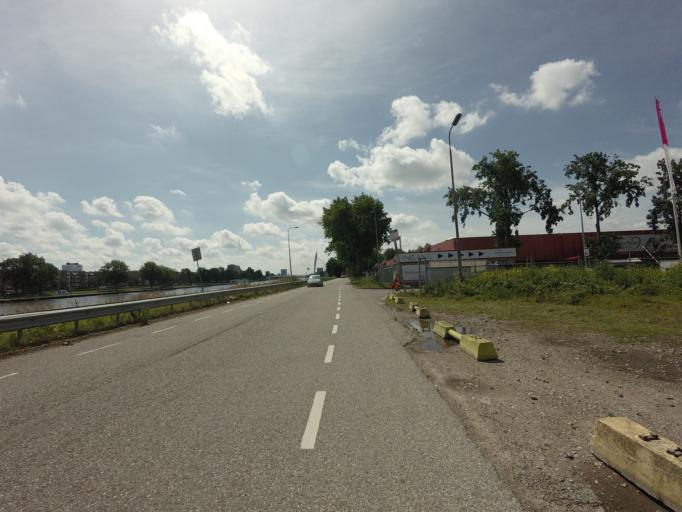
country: NL
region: Utrecht
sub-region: Gemeente Utrecht
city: Utrecht
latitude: 52.0785
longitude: 5.0805
